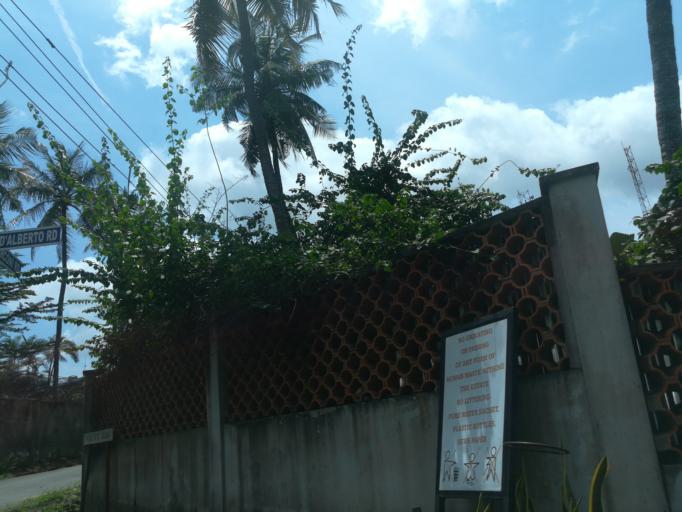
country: NG
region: Lagos
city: Somolu
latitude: 6.5419
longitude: 3.3662
